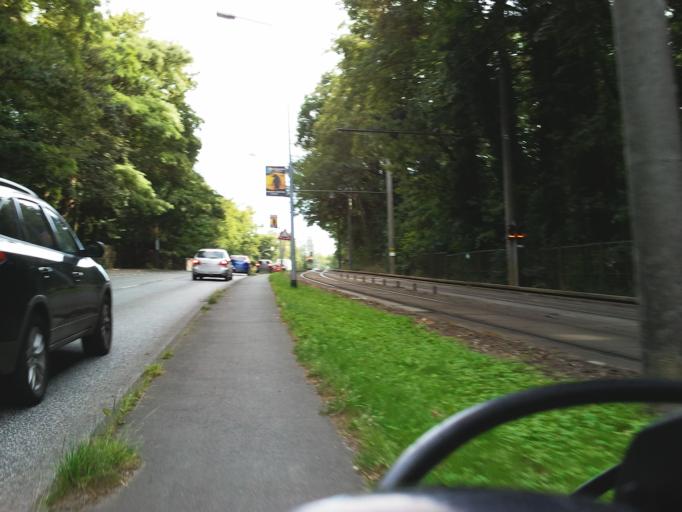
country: DE
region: Mecklenburg-Vorpommern
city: Kritzmow
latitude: 54.0771
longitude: 12.0875
